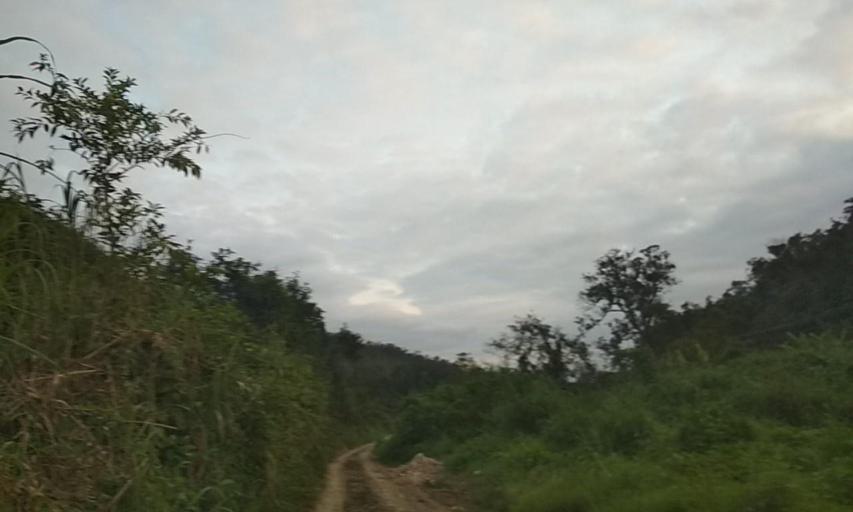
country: MX
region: Veracruz
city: Papantla de Olarte
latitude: 20.4257
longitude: -97.3345
